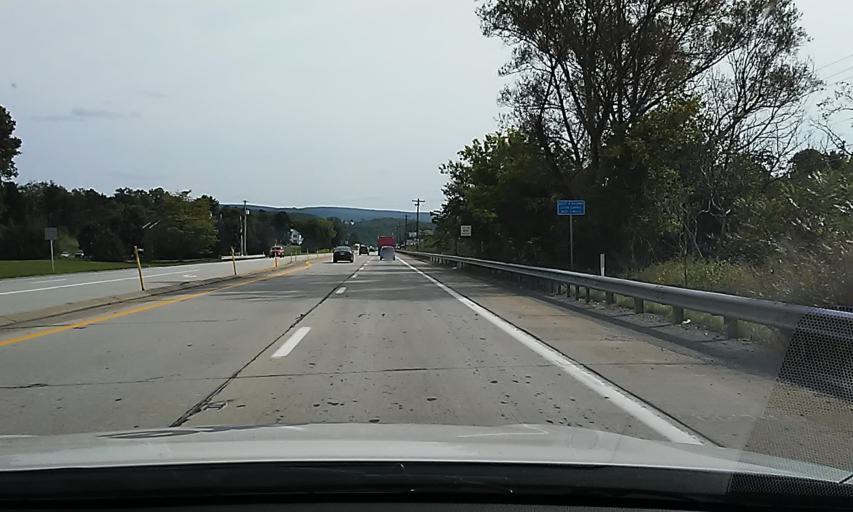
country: US
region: Pennsylvania
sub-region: Westmoreland County
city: Scottdale
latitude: 40.0674
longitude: -79.5645
